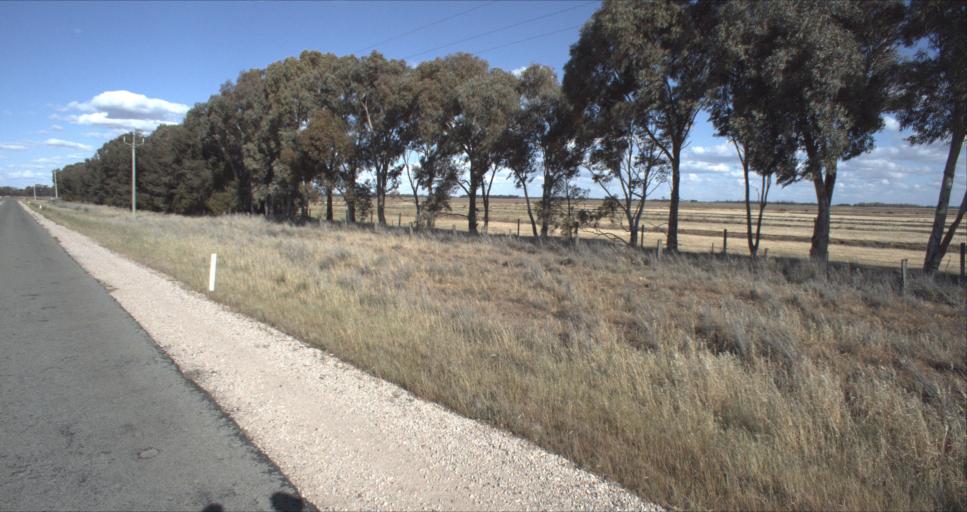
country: AU
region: New South Wales
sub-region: Leeton
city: Leeton
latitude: -34.4586
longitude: 146.2661
